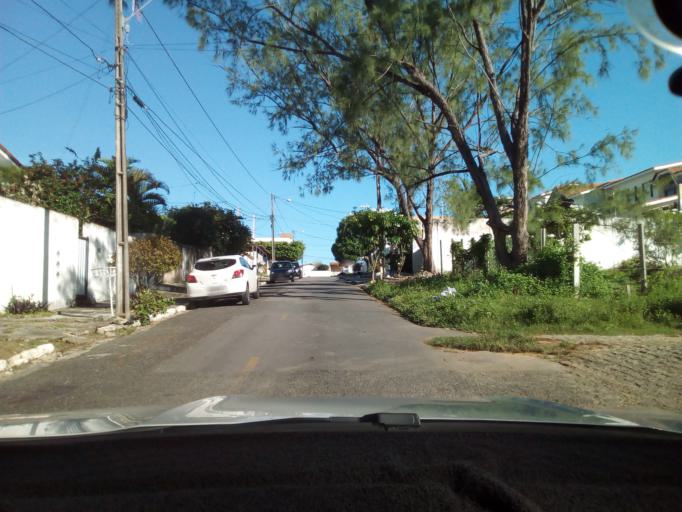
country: BR
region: Paraiba
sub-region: Joao Pessoa
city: Joao Pessoa
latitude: -7.1348
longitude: -34.8335
